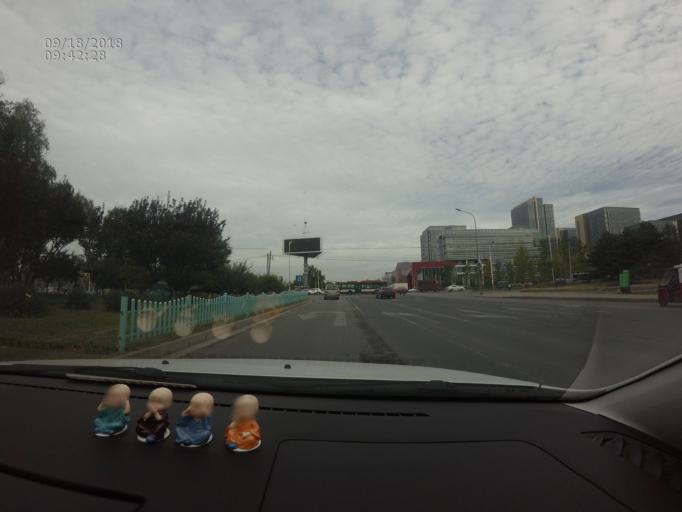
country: CN
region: Beijing
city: Xibeiwang
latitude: 40.0717
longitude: 116.2384
